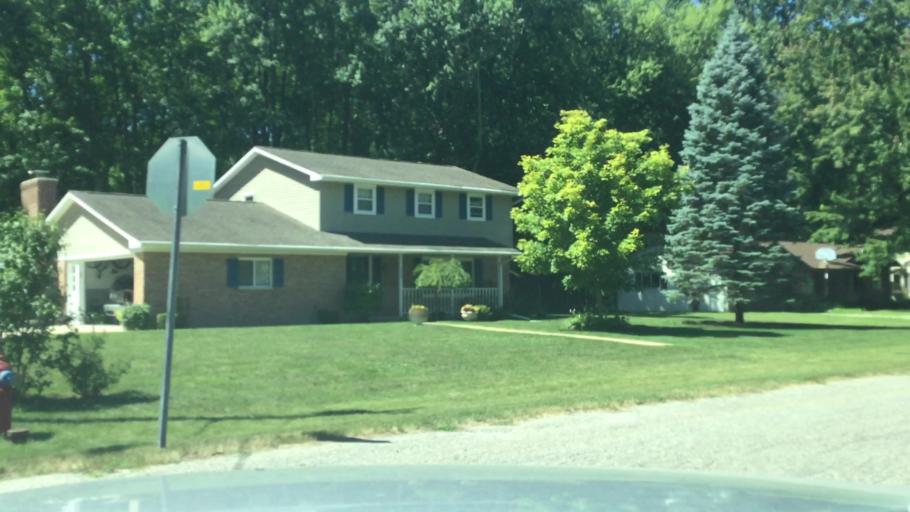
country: US
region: Michigan
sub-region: Saginaw County
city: Shields
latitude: 43.4199
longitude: -84.0674
